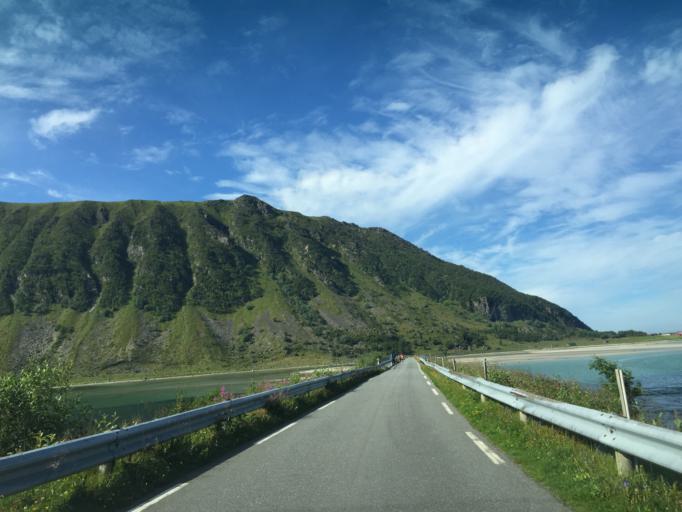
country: NO
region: Nordland
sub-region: Vagan
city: Svolvaer
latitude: 68.3945
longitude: 14.5577
